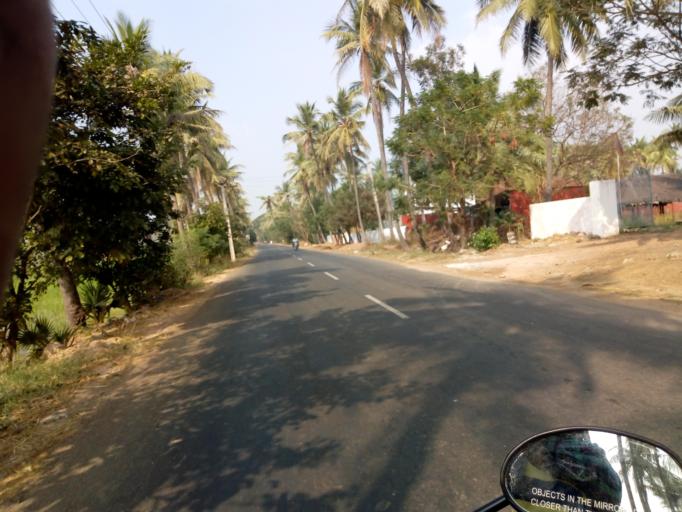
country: IN
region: Andhra Pradesh
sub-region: West Godavari
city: Palakollu
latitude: 16.5838
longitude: 81.6437
